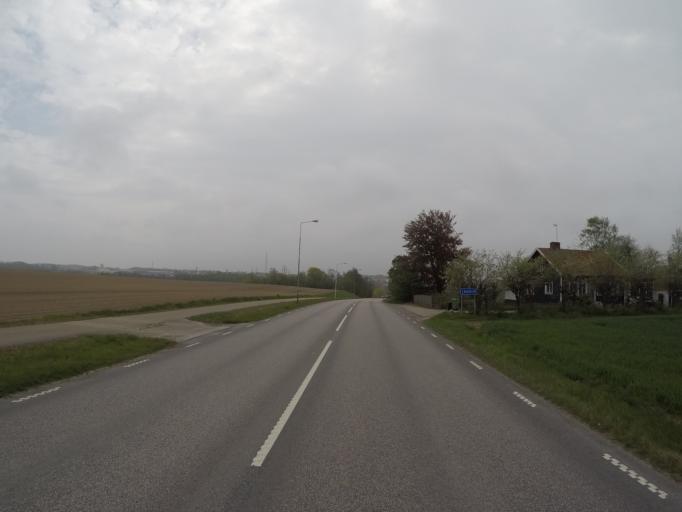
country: SE
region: Halland
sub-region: Laholms Kommun
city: Laholm
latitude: 56.5208
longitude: 13.0550
